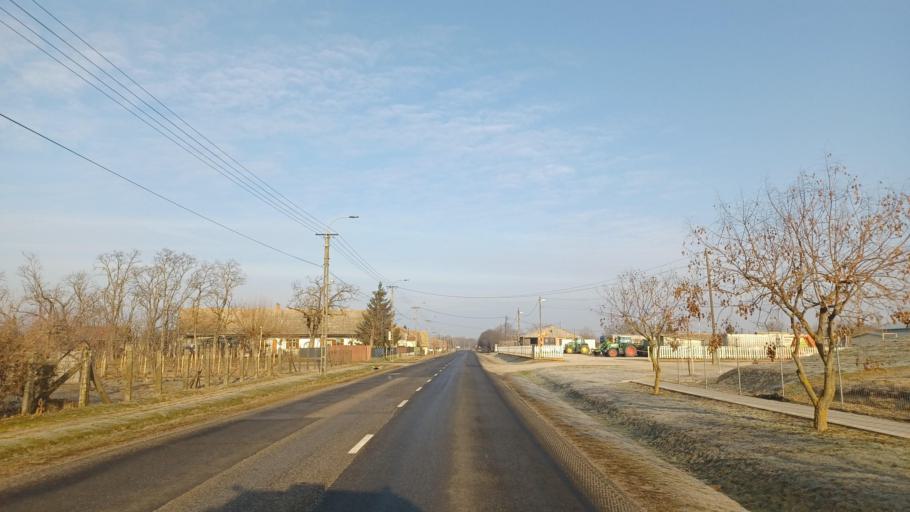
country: HU
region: Fejer
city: Cece
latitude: 46.7202
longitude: 18.6631
